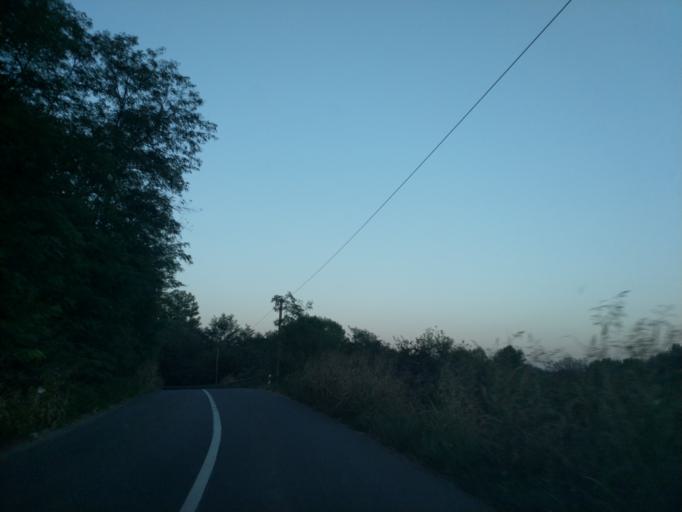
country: RS
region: Central Serbia
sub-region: Rasinski Okrug
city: Krusevac
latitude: 43.6222
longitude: 21.3261
